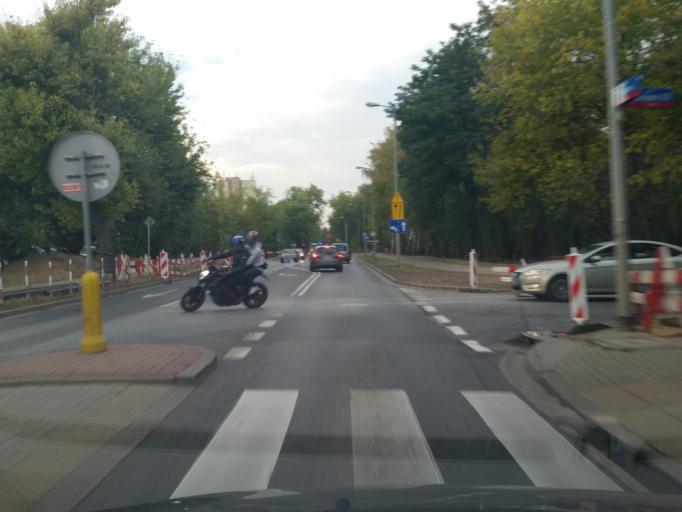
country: PL
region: Masovian Voivodeship
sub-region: Warszawa
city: Bemowo
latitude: 52.2465
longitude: 20.8977
